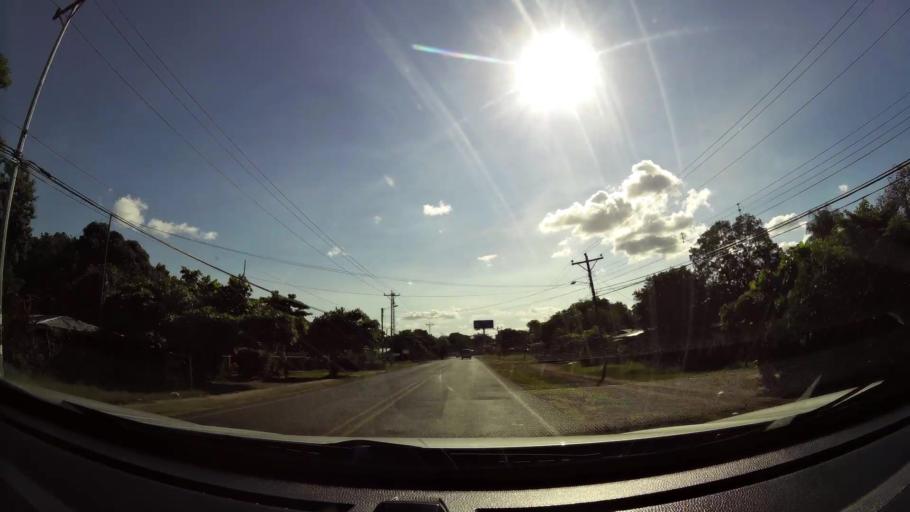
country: CR
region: Guanacaste
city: Sardinal
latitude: 10.5662
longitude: -85.5888
